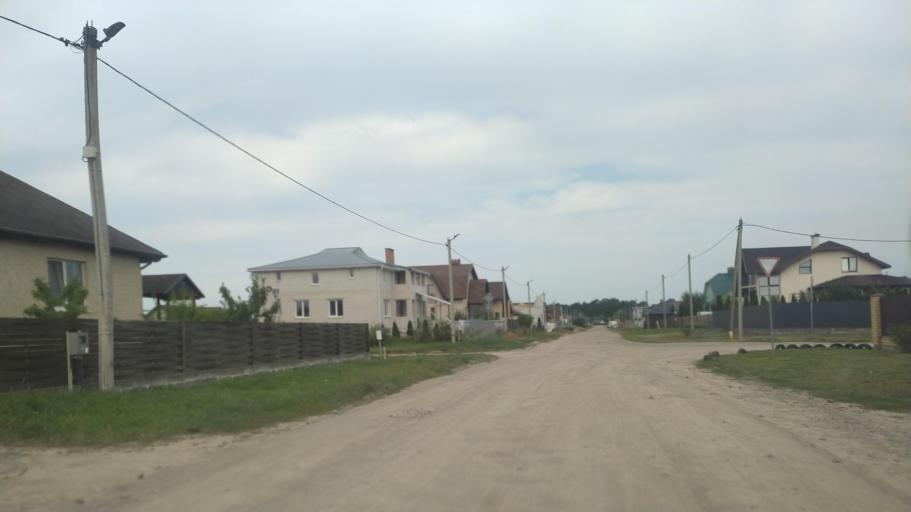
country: BY
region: Brest
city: Byaroza
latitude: 52.5420
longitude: 24.9691
